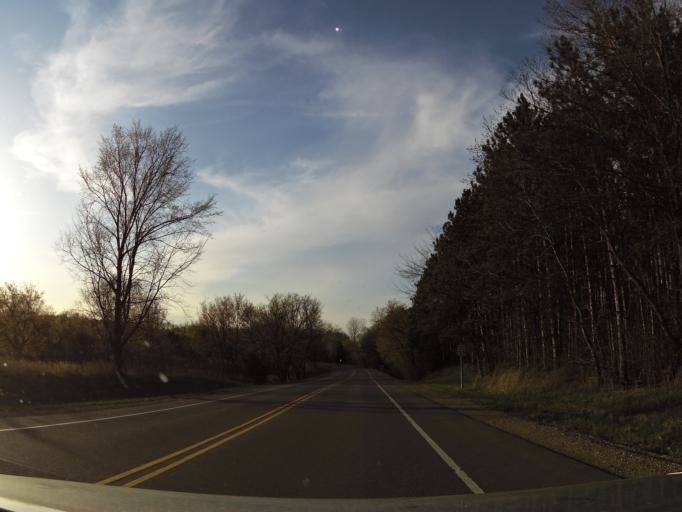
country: US
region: Minnesota
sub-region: Washington County
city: Lake Saint Croix Beach
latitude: 44.9177
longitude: -92.6855
